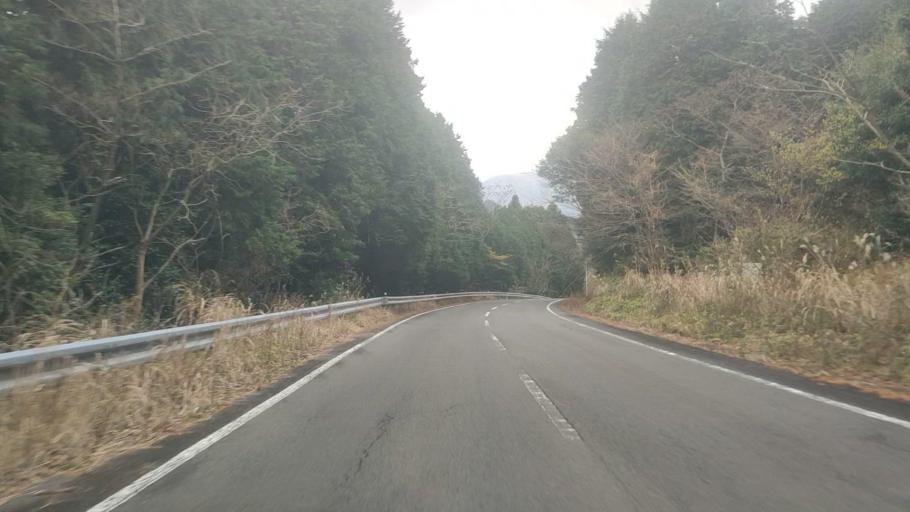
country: JP
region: Nagasaki
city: Shimabara
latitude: 32.7917
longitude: 130.2817
